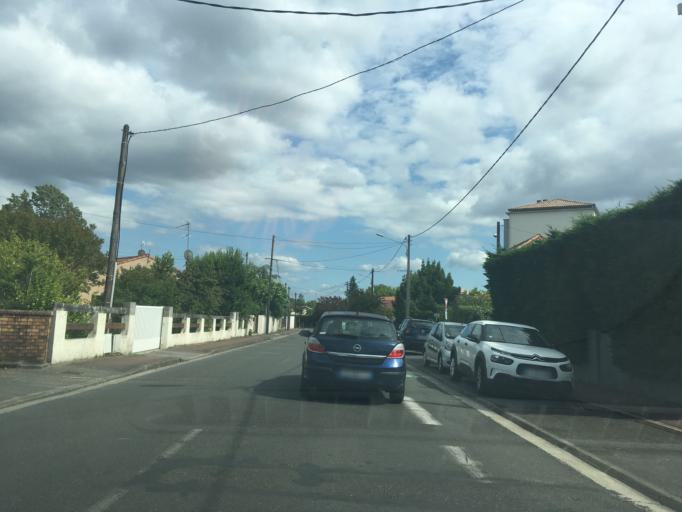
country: FR
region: Aquitaine
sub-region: Departement de la Gironde
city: Merignac
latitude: 44.8490
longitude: -0.6413
